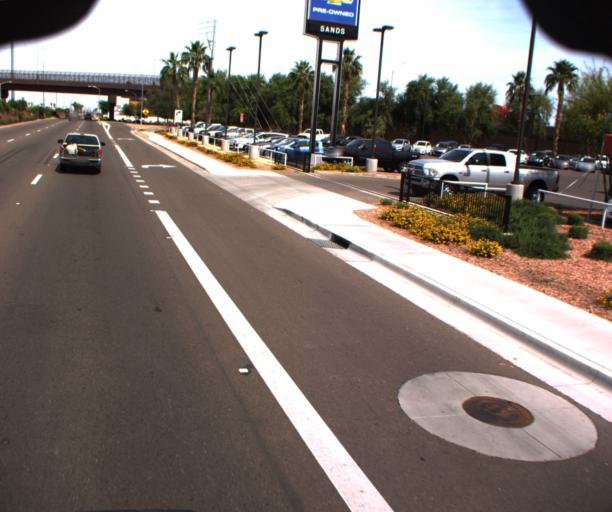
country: US
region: Arizona
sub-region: Maricopa County
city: Glendale
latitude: 33.5305
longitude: -112.1762
